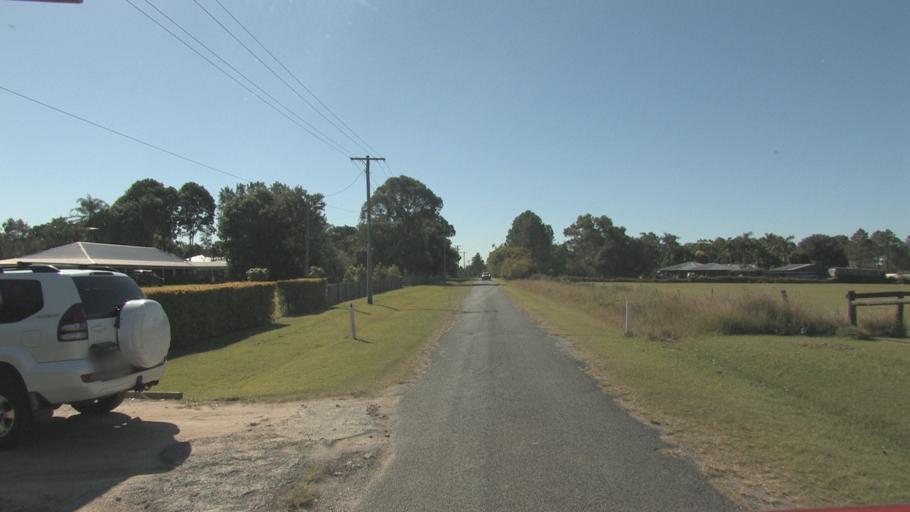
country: AU
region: Queensland
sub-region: Logan
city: Waterford West
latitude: -27.7176
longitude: 153.1263
